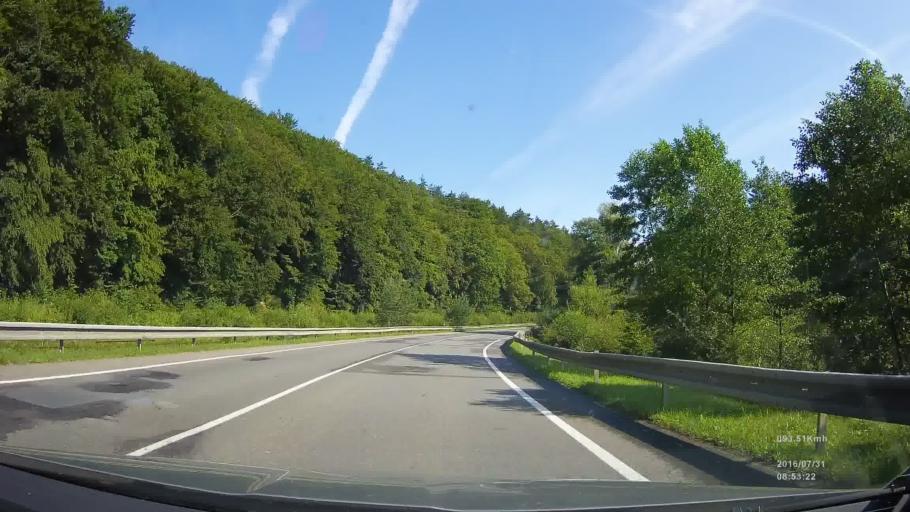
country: SK
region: Presovsky
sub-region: Okres Presov
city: Presov
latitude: 49.1263
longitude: 21.3107
